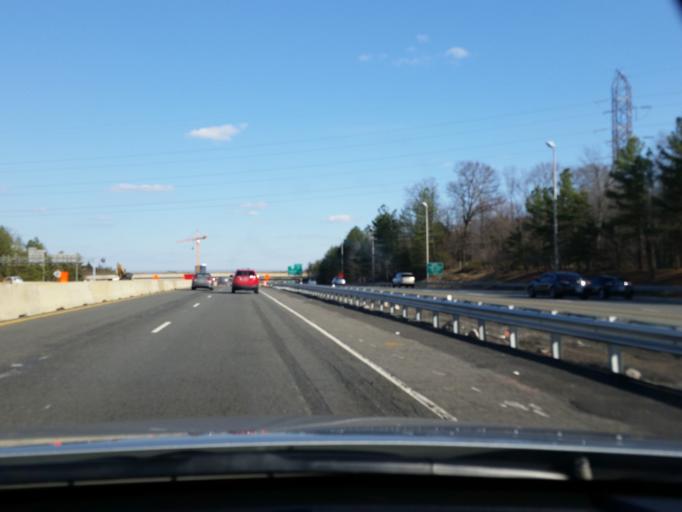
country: US
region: Virginia
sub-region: Fairfax County
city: Herndon
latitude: 38.9539
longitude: -77.3928
